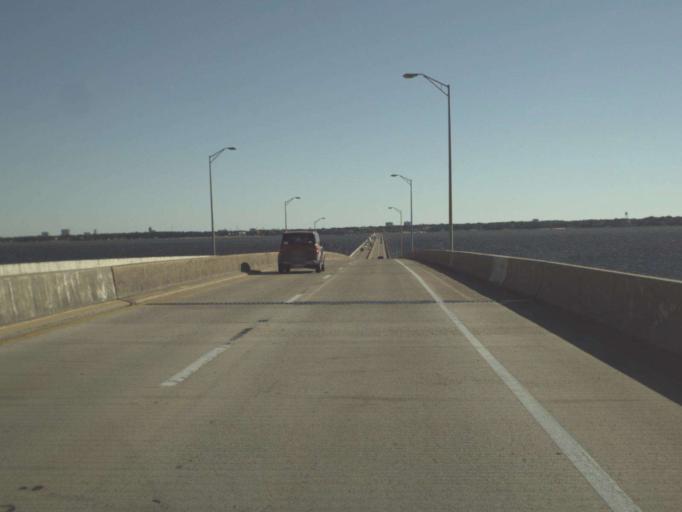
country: US
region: Florida
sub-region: Escambia County
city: East Pensacola Heights
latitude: 30.3941
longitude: -87.1849
